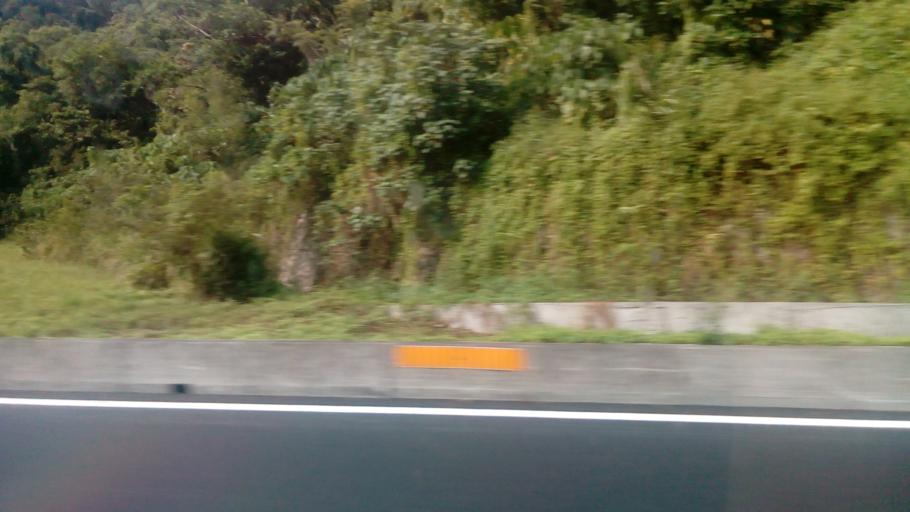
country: TW
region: Taiwan
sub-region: Yilan
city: Yilan
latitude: 24.5909
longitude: 121.8595
